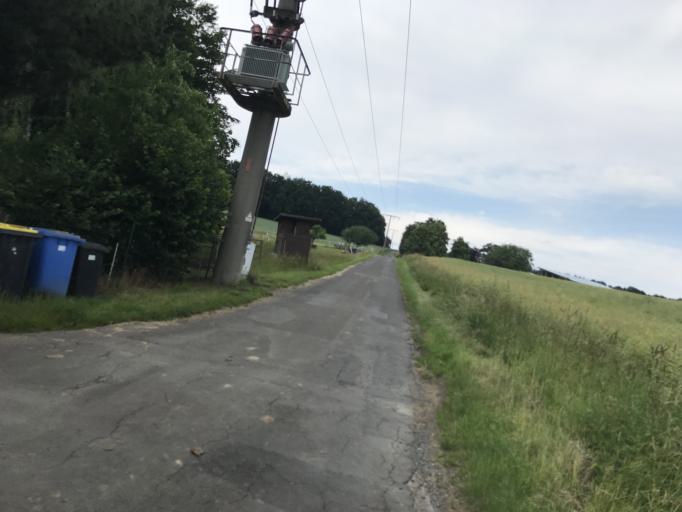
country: DE
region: Hesse
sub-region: Regierungsbezirk Giessen
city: Laubach
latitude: 50.5268
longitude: 8.9696
